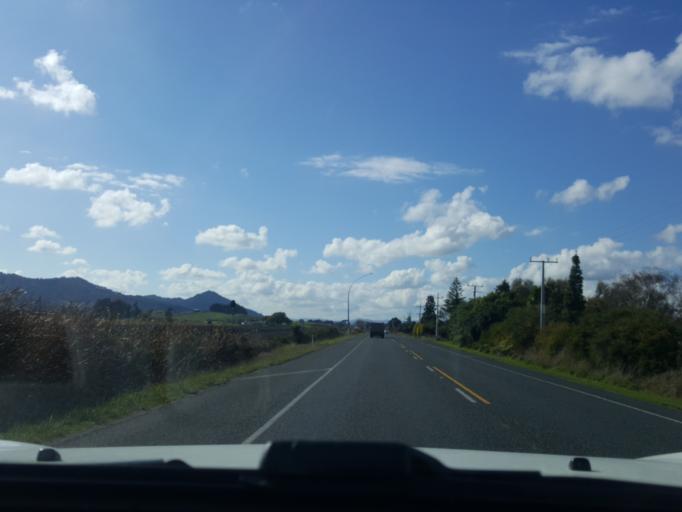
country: NZ
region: Waikato
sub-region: Waikato District
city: Ngaruawahia
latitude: -37.6550
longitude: 175.1549
